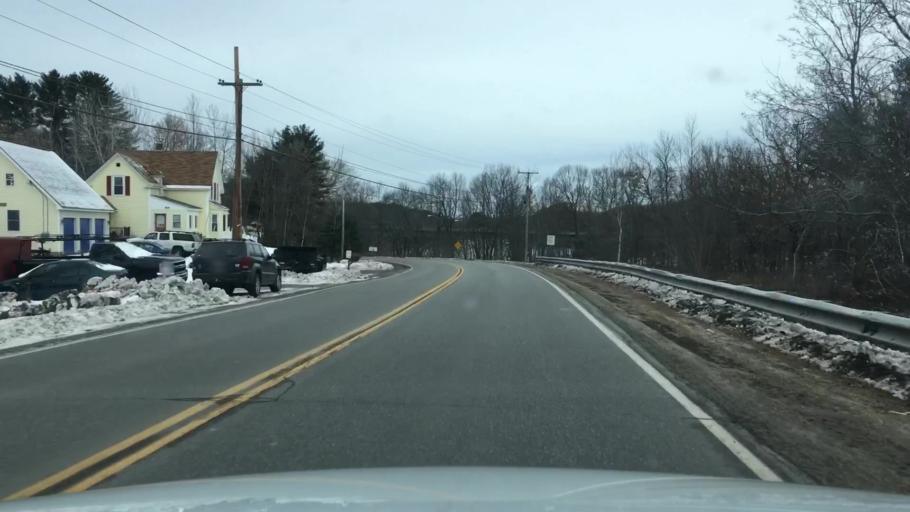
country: US
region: Maine
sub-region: Androscoggin County
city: Lewiston
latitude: 44.0609
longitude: -70.2063
